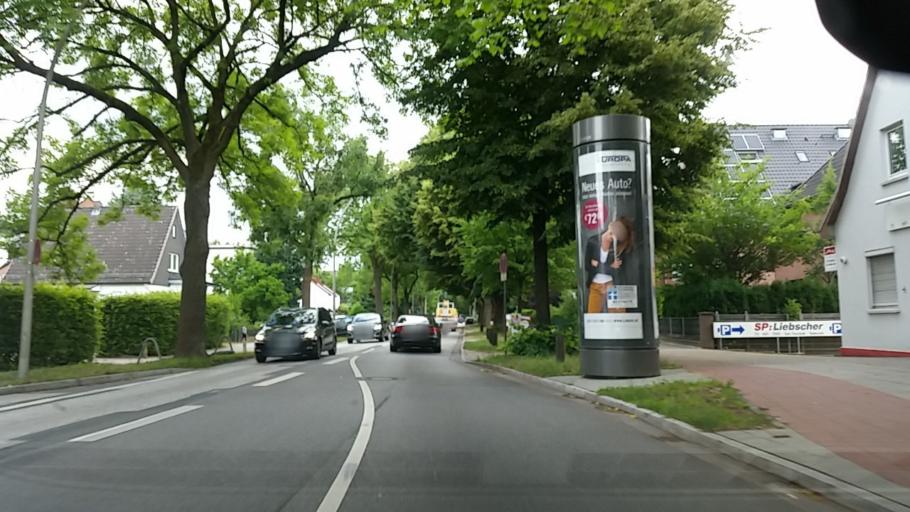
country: DE
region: Hamburg
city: Eidelstedt
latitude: 53.6276
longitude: 9.9099
